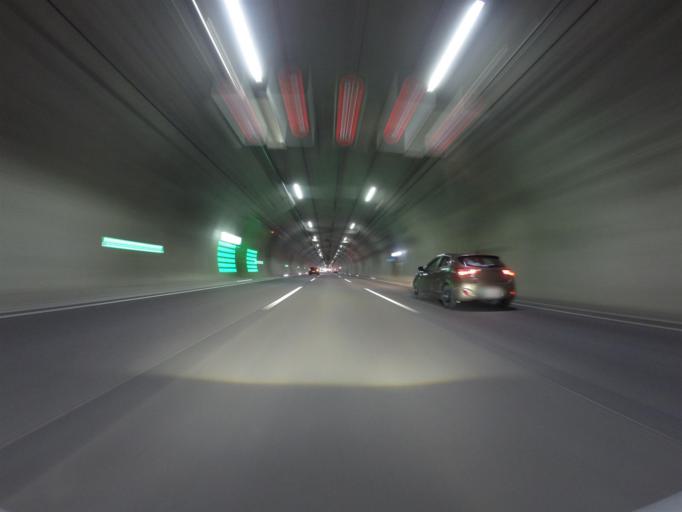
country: DE
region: Thuringia
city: Bucha
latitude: 50.8747
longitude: 11.5599
